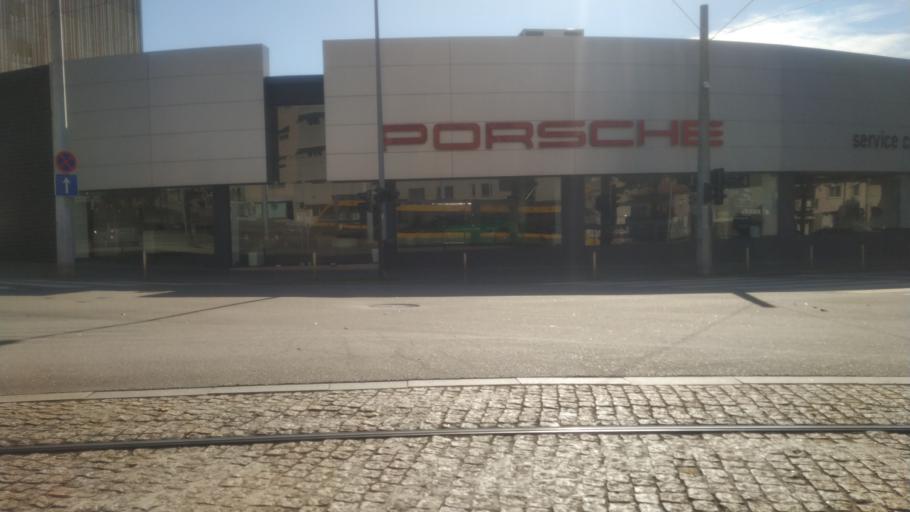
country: PT
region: Porto
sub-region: Matosinhos
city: Matosinhos
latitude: 41.1791
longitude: -8.6783
